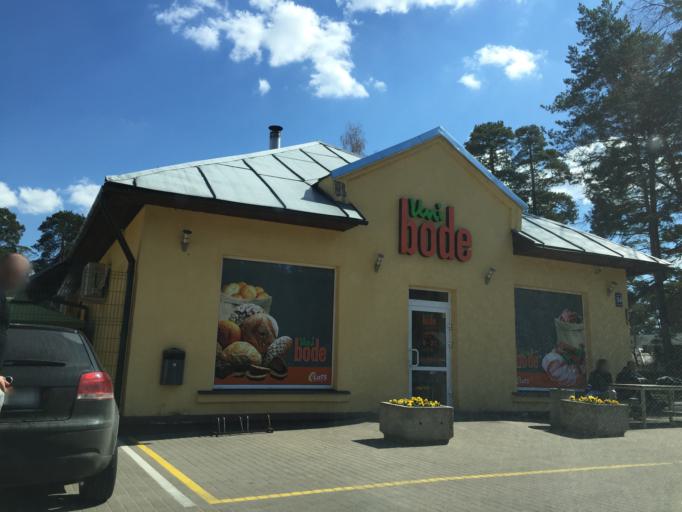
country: LV
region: Saulkrastu
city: Saulkrasti
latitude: 57.2438
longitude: 24.4027
